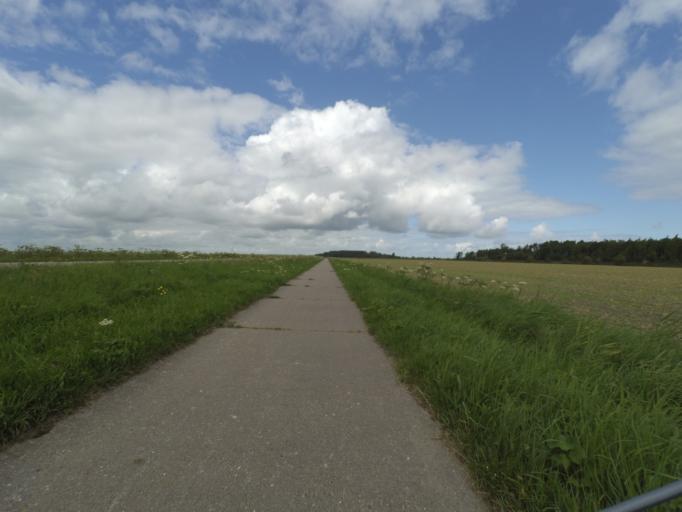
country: NL
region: Groningen
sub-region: Gemeente Zuidhorn
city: Grijpskerk
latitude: 53.3180
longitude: 6.2542
